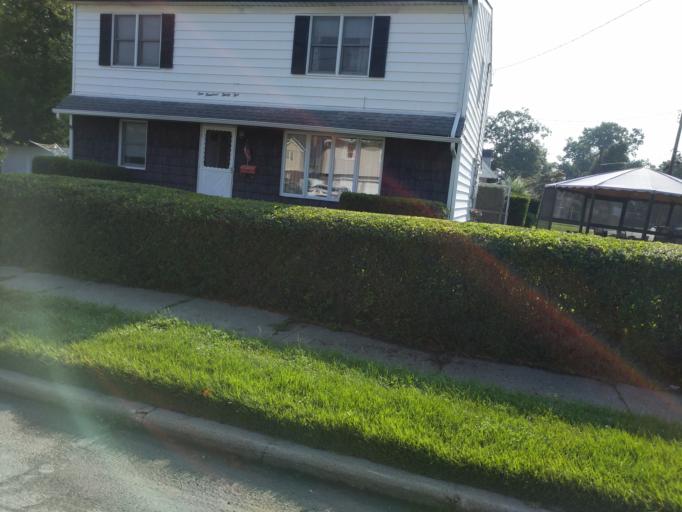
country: US
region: New York
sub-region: Nassau County
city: Valley Stream
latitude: 40.6556
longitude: -73.7051
